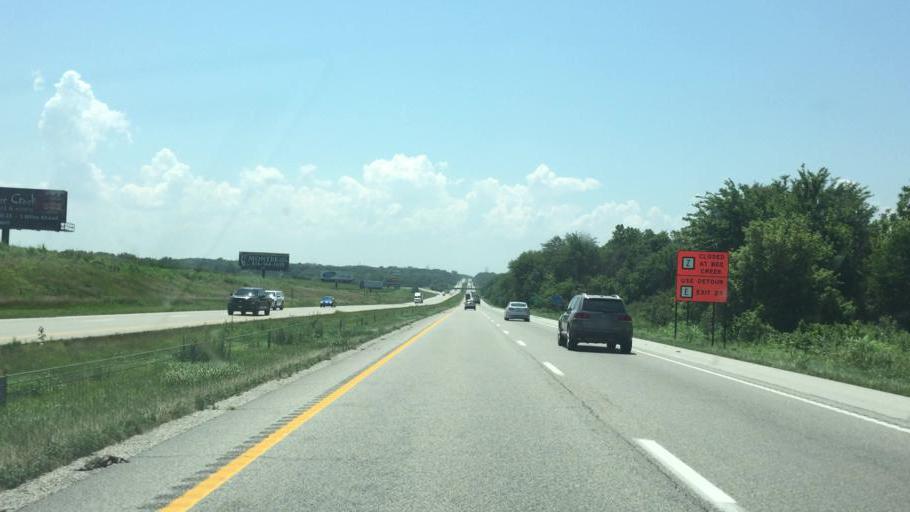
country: US
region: Missouri
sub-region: Platte County
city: Platte City
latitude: 39.5269
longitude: -94.7872
